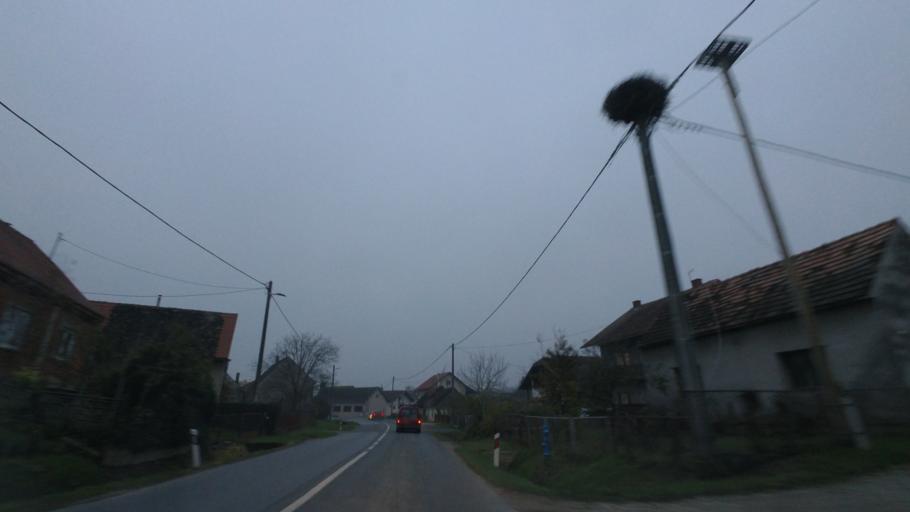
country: HR
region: Sisacko-Moslavacka
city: Petrinja
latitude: 45.4541
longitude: 16.2559
